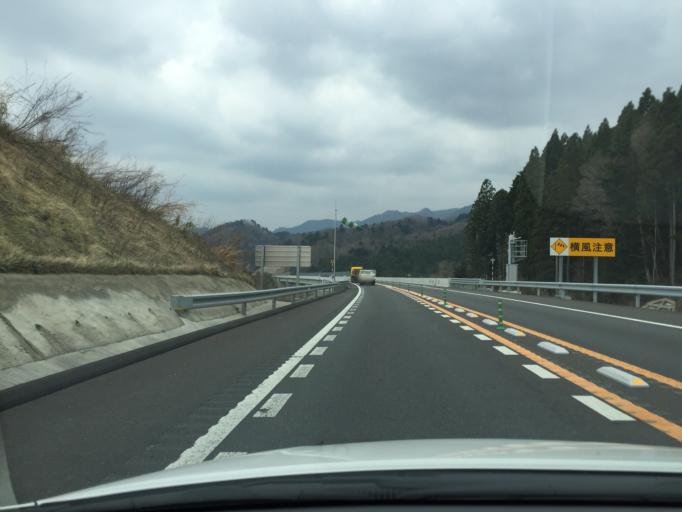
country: JP
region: Miyagi
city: Marumori
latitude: 37.8273
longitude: 140.8755
